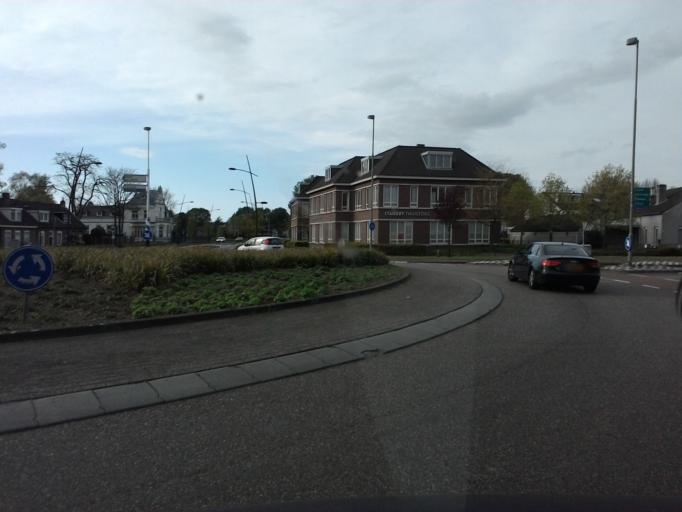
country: NL
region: North Brabant
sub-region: Gemeente Boxtel
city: Boxtel
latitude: 51.5965
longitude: 5.3245
